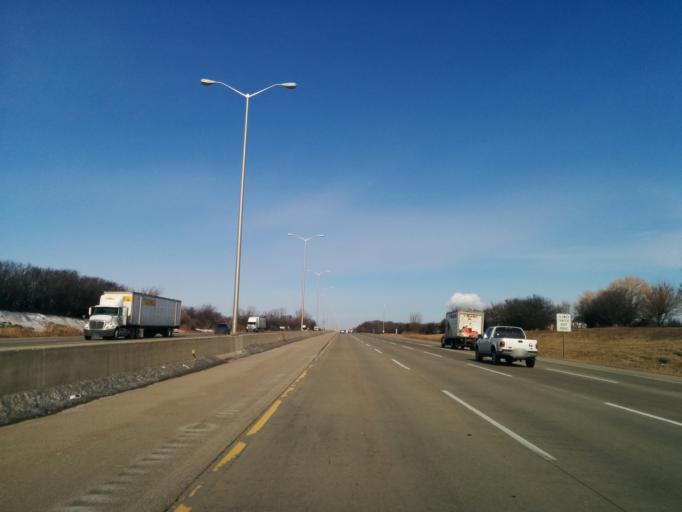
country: US
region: Illinois
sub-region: Lake County
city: Grandwood Park
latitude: 42.3952
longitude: -87.9488
